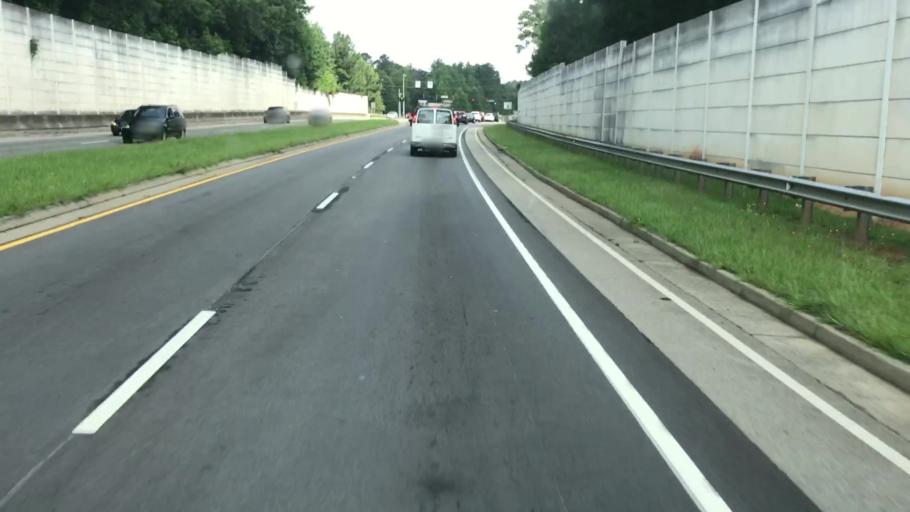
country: US
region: Georgia
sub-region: Gwinnett County
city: Duluth
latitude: 33.9739
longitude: -84.0728
